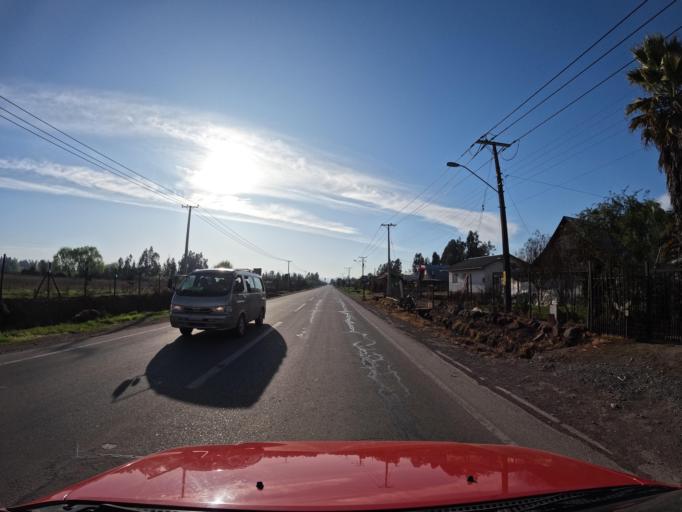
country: CL
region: Maule
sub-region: Provincia de Curico
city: Teno
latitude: -34.8891
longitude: -71.0705
